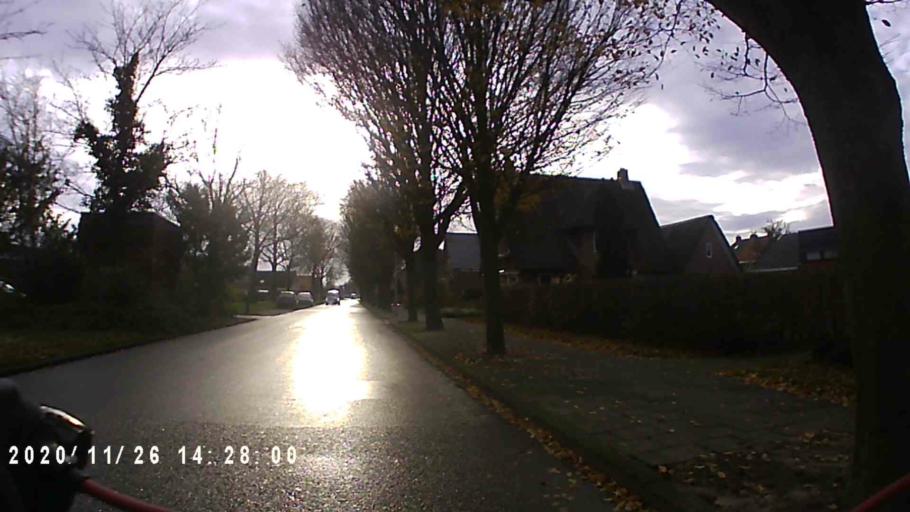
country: NL
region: Groningen
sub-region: Gemeente Appingedam
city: Appingedam
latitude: 53.3199
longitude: 6.8686
